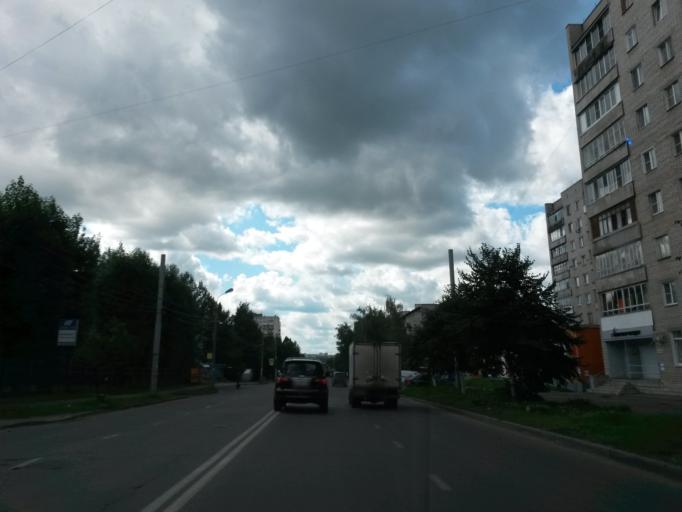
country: RU
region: Jaroslavl
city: Yaroslavl
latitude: 57.6245
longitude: 39.8485
